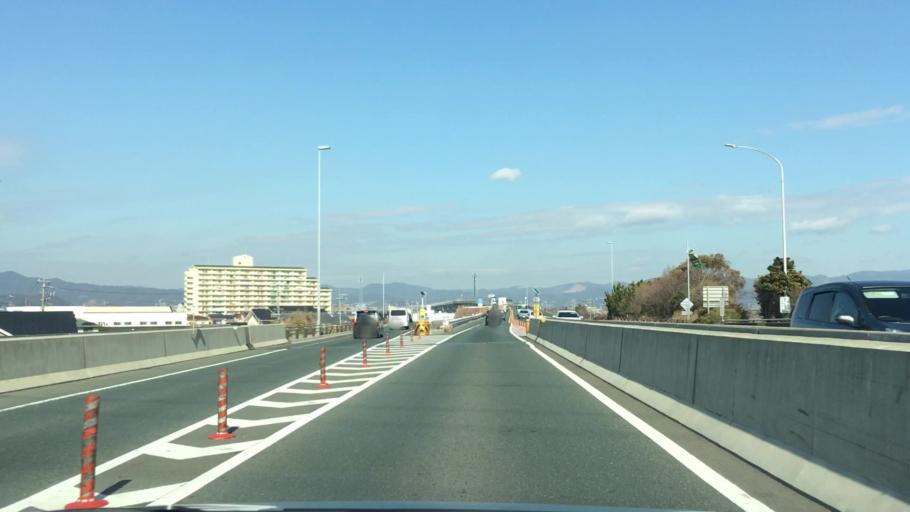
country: JP
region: Aichi
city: Kozakai-cho
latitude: 34.7803
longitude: 137.3327
